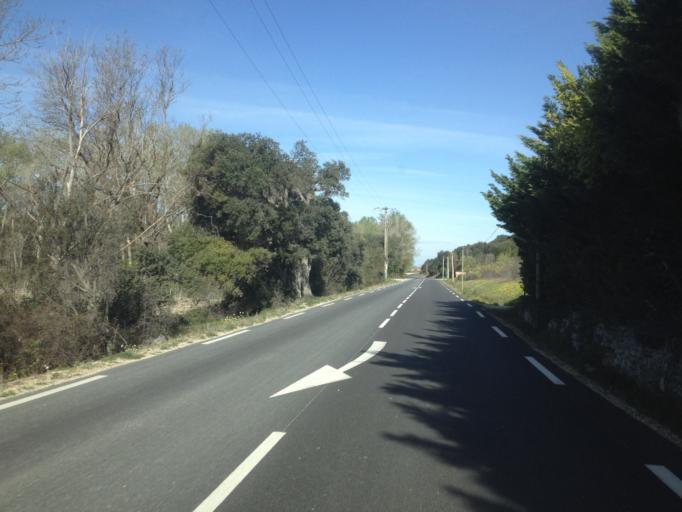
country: FR
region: Languedoc-Roussillon
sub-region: Departement du Gard
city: Roquemaure
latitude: 44.0639
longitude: 4.7947
